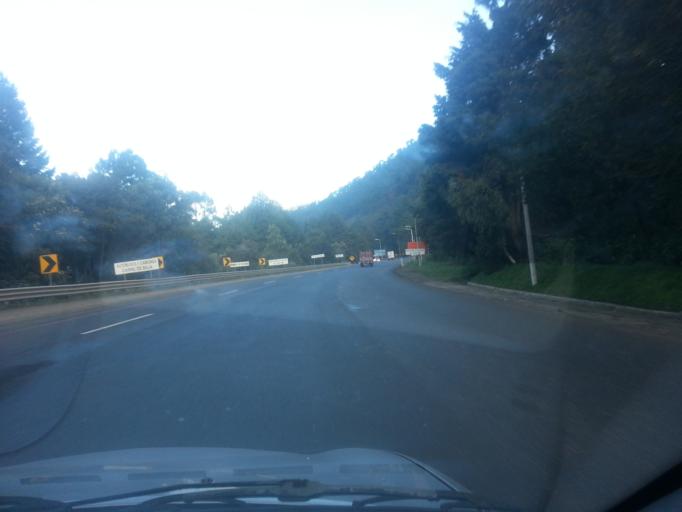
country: MX
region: Morelos
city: San Jeronimo Acazulco
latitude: 19.2977
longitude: -99.4070
